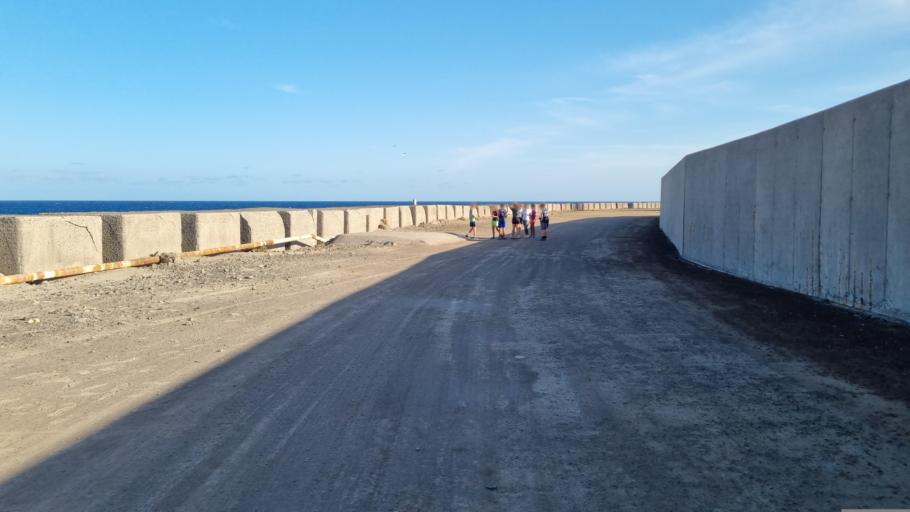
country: ES
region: Canary Islands
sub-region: Provincia de Santa Cruz de Tenerife
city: San Isidro
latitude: 28.0872
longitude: -16.4908
